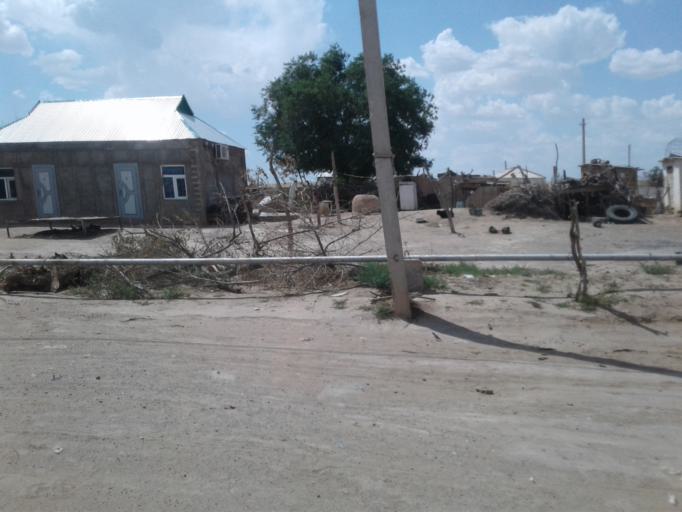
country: TM
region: Ahal
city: Abadan
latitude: 38.7640
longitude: 58.4925
